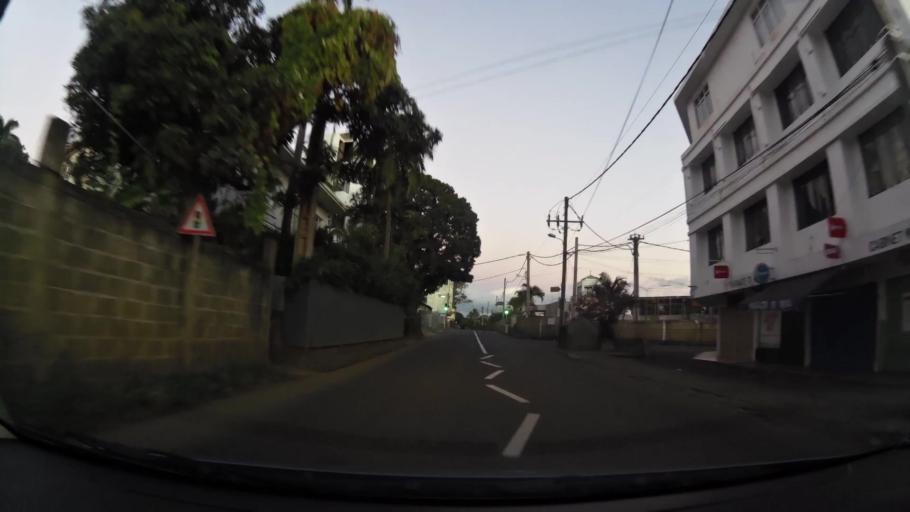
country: MU
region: Moka
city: Moka
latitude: -20.2217
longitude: 57.5025
